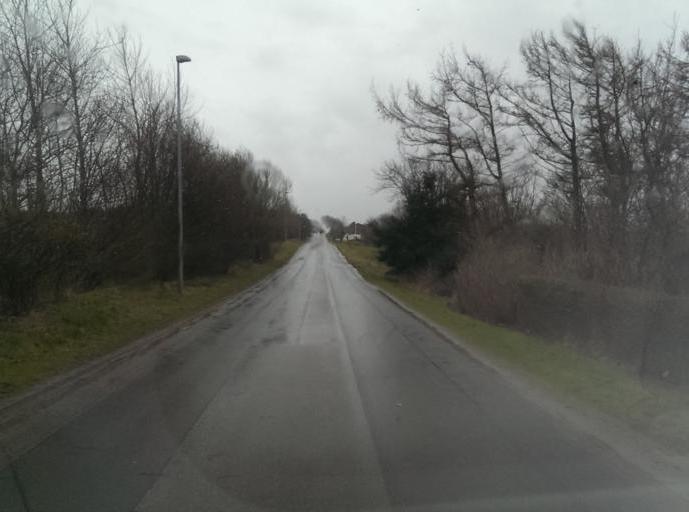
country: DK
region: Central Jutland
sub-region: Ringkobing-Skjern Kommune
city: Skjern
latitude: 56.0046
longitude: 8.4169
